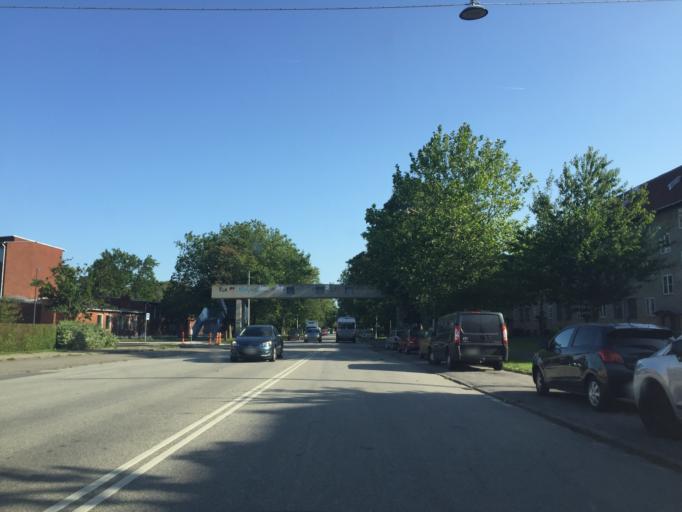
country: DK
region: Capital Region
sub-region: Frederiksberg Kommune
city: Frederiksberg
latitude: 55.7190
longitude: 12.5434
